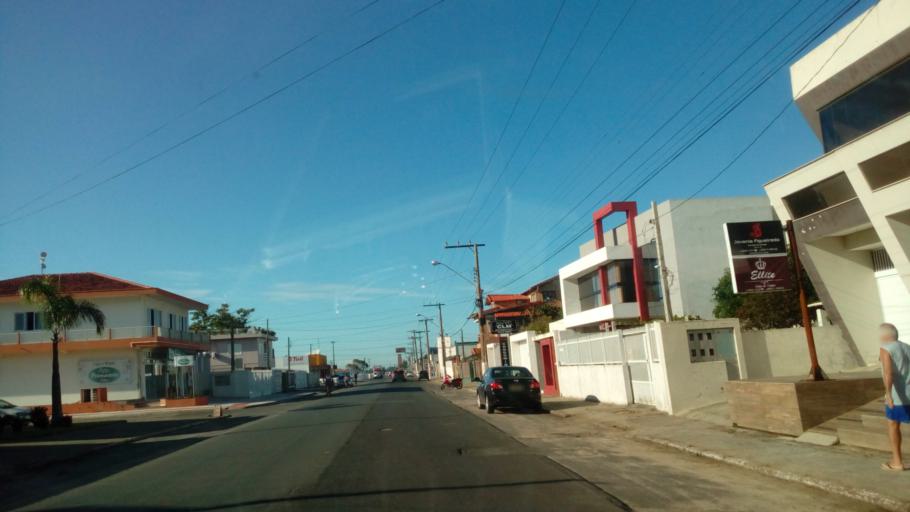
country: BR
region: Santa Catarina
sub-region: Laguna
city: Laguna
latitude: -28.4918
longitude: -48.7721
